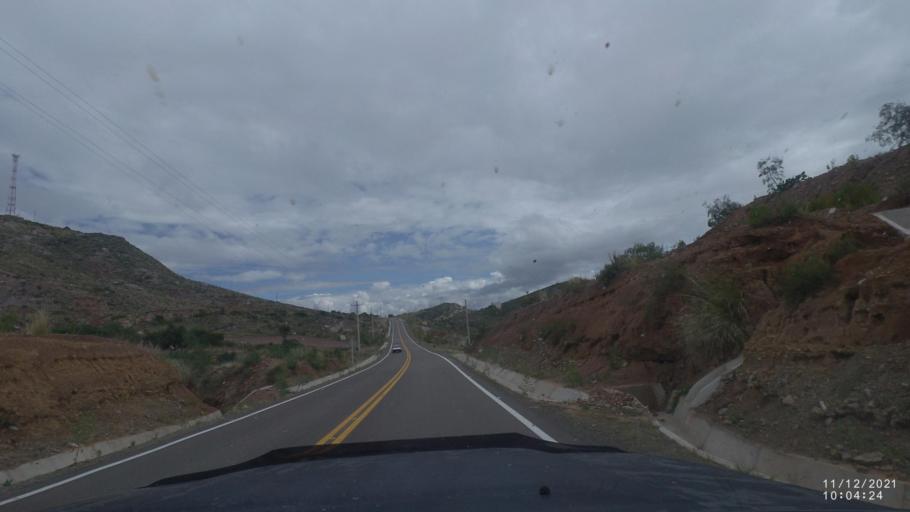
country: BO
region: Cochabamba
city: Cliza
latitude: -17.7108
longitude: -65.9425
